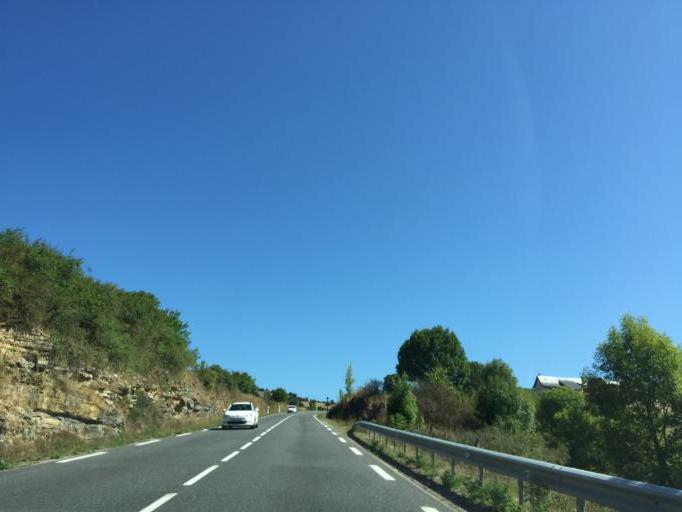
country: FR
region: Midi-Pyrenees
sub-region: Departement de l'Aveyron
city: Saint-Georges-de-Luzencon
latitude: 44.0127
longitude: 2.9849
